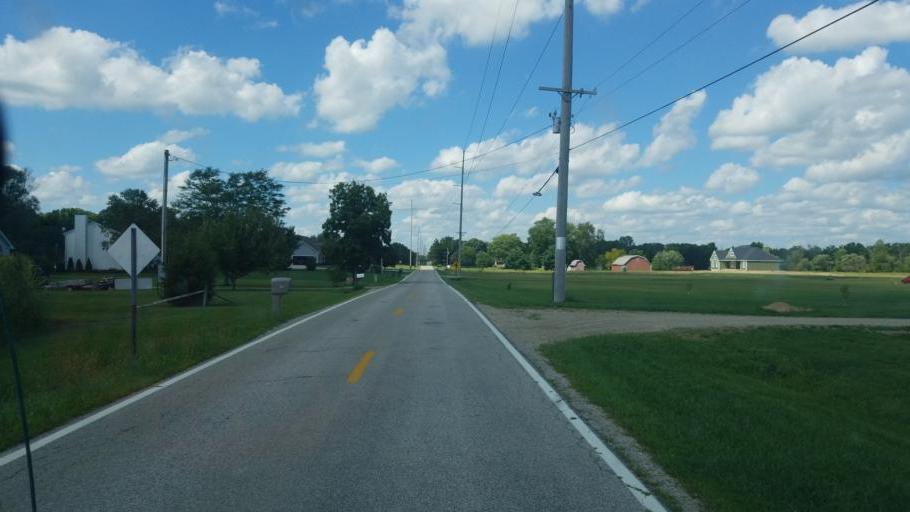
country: US
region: Ohio
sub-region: Delaware County
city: Delaware
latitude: 40.3166
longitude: -83.2009
